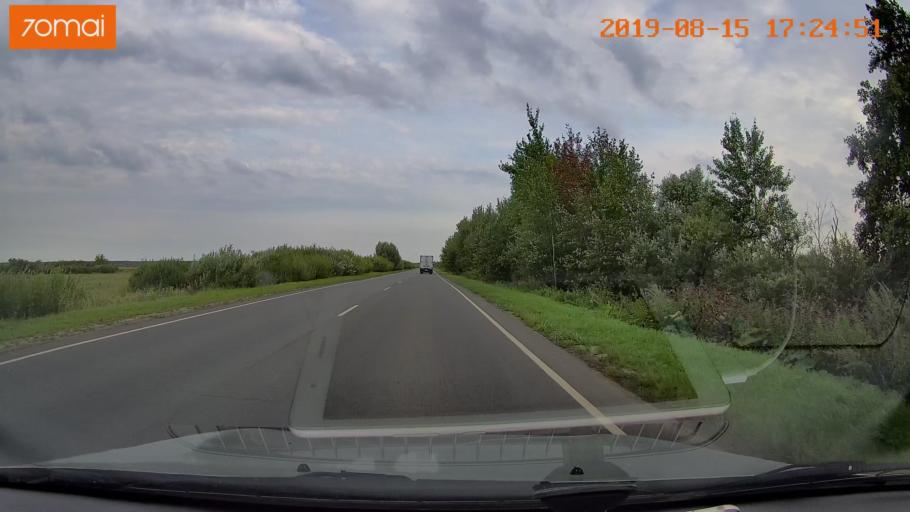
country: RU
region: Moskovskaya
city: Ashitkovo
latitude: 55.3819
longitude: 38.5587
